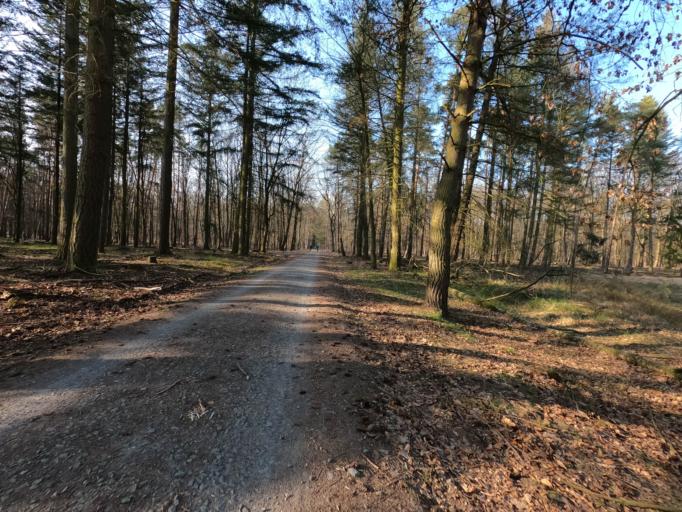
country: DE
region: Hesse
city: Raunheim
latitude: 50.0060
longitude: 8.5069
